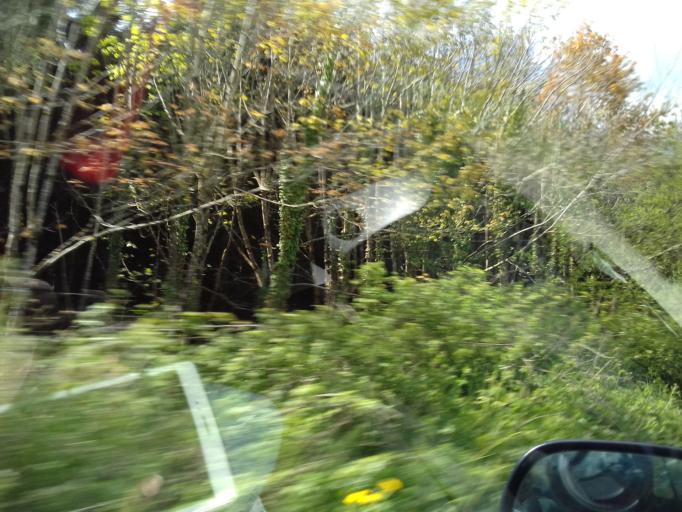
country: IE
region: Leinster
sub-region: Loch Garman
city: Loch Garman
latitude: 52.2825
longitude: -6.6683
